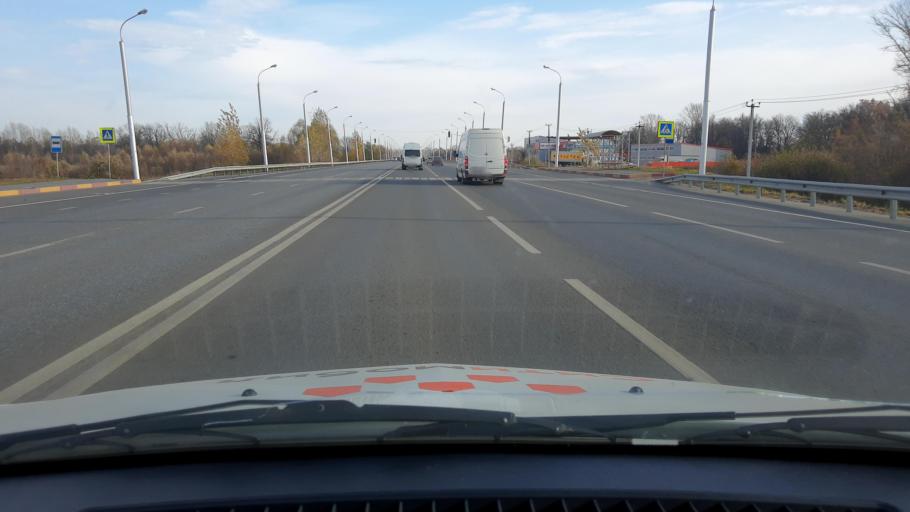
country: RU
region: Bashkortostan
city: Ufa
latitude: 54.8052
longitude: 56.1809
